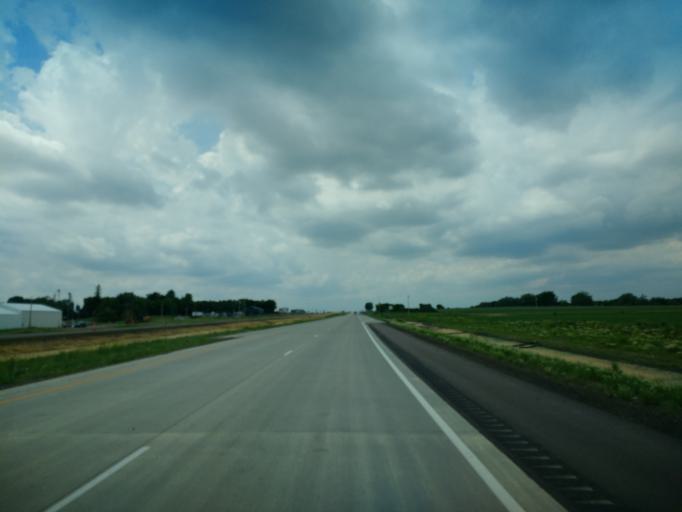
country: US
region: Minnesota
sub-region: Cottonwood County
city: Windom
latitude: 43.9101
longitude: -95.0354
